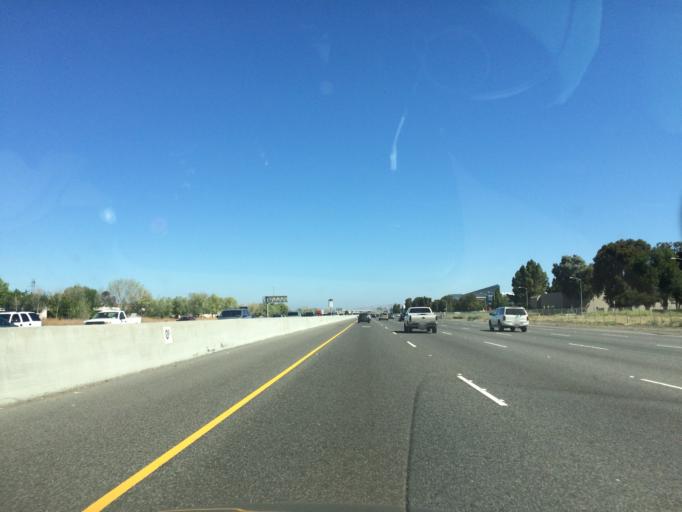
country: US
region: California
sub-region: Santa Clara County
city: Milpitas
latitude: 37.4653
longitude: -121.9271
